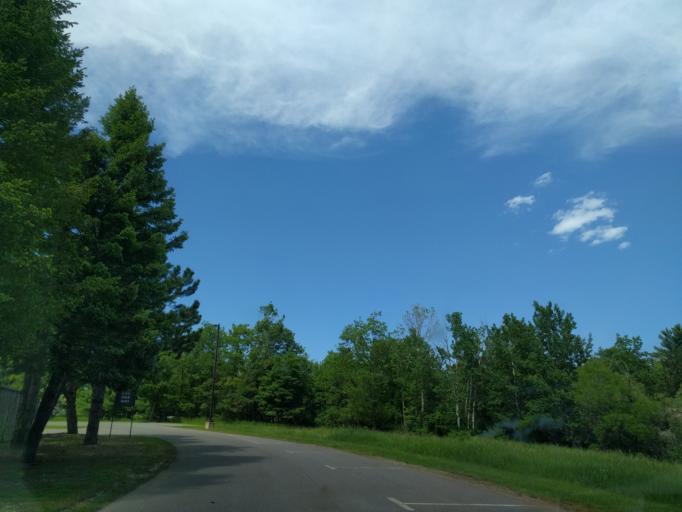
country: US
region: Michigan
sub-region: Marquette County
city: Marquette
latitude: 46.5704
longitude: -87.4017
